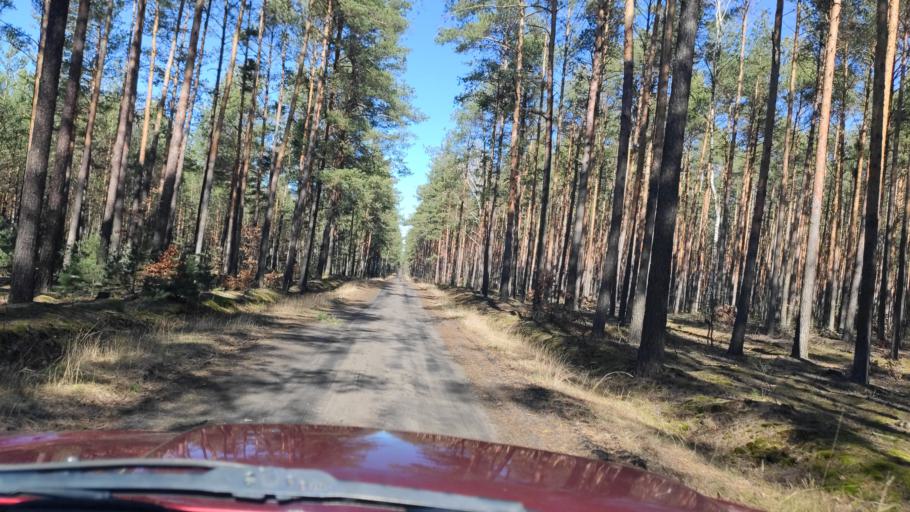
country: PL
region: Masovian Voivodeship
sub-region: Powiat zwolenski
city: Zwolen
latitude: 51.4254
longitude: 21.5505
